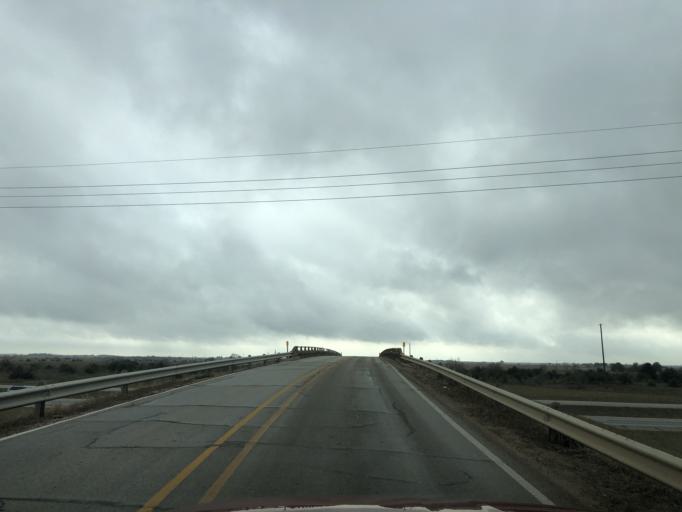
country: US
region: Texas
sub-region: Austin County
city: Sealy
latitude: 29.7595
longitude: -96.2209
